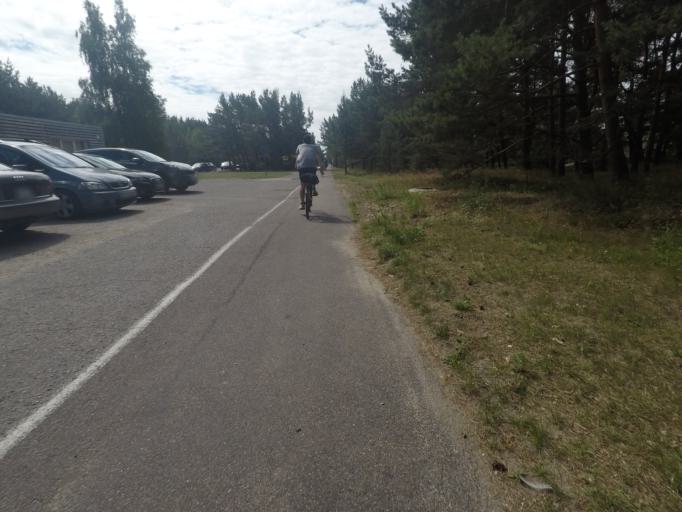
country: LT
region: Klaipedos apskritis
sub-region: Klaipeda
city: Klaipeda
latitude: 55.5455
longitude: 21.1006
